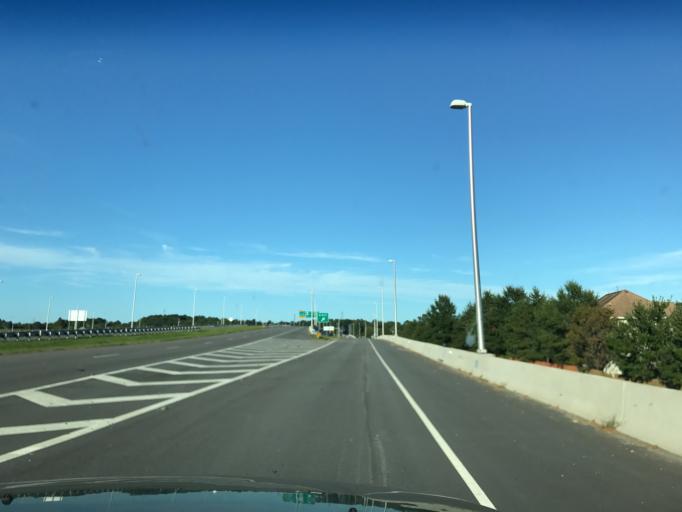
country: US
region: Virginia
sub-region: City of Chesapeake
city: Chesapeake
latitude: 36.7450
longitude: -76.2866
